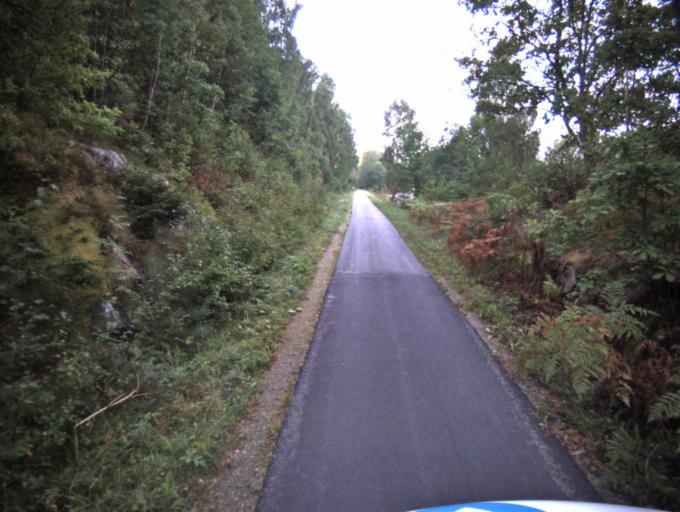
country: SE
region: Vaestra Goetaland
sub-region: Ulricehamns Kommun
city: Ulricehamn
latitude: 57.7538
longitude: 13.3963
